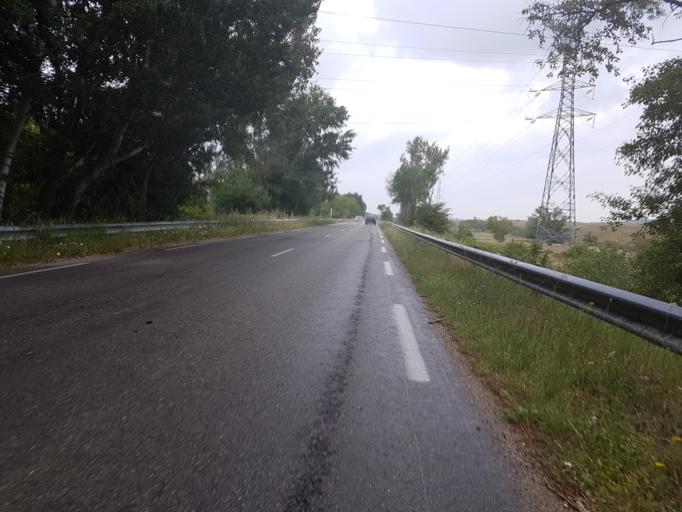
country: FR
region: Languedoc-Roussillon
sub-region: Departement du Gard
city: Villeneuve-les-Avignon
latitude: 43.9885
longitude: 4.8220
